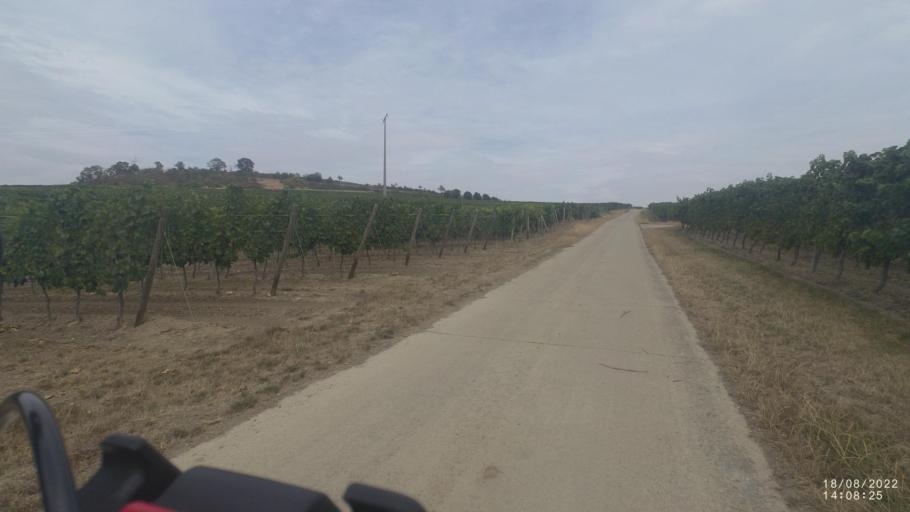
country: DE
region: Rheinland-Pfalz
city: Vendersheim
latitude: 49.8594
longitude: 8.0783
